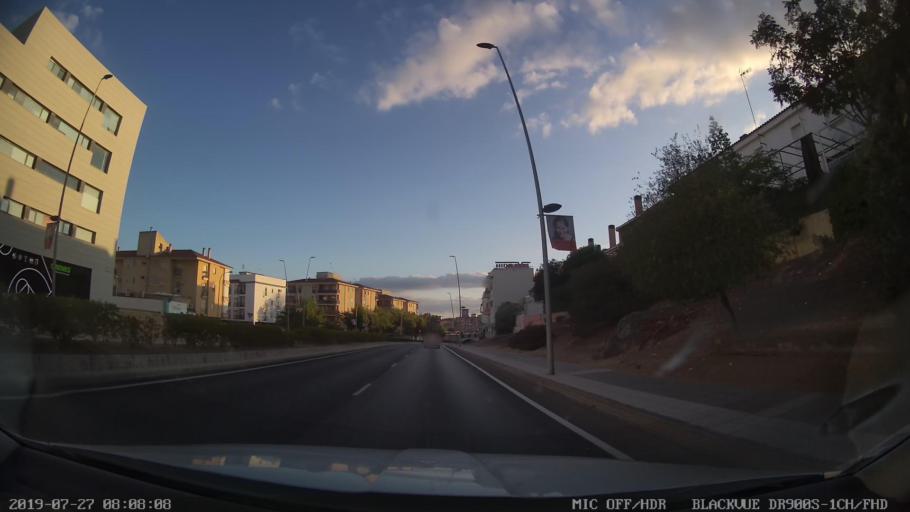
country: ES
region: Extremadura
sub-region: Provincia de Badajoz
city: Merida
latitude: 38.9139
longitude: -6.3341
